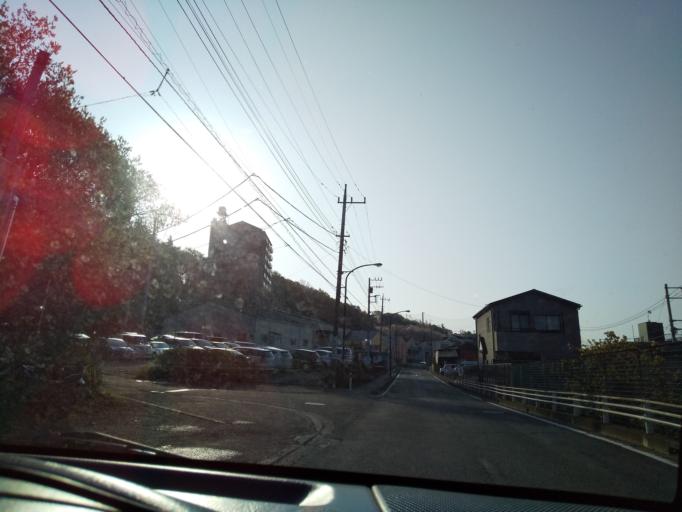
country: JP
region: Kanagawa
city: Zama
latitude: 35.5535
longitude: 139.3673
